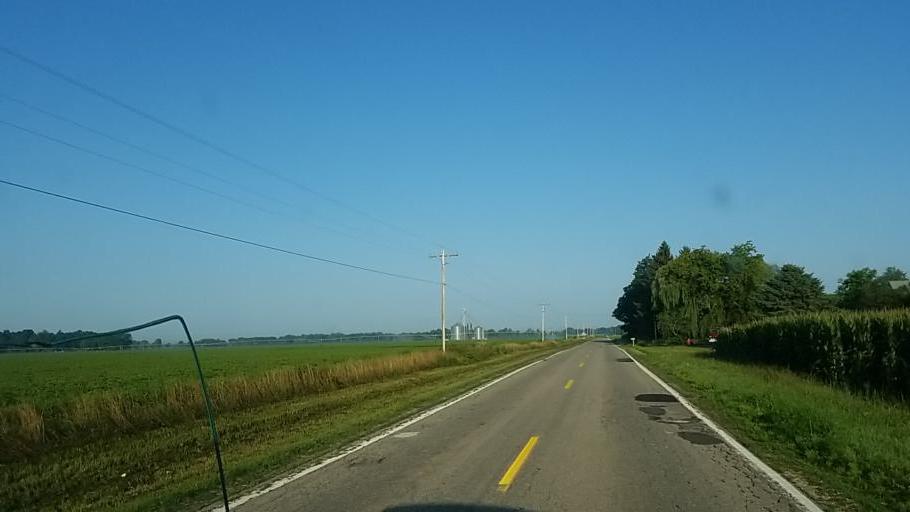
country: US
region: Michigan
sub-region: Montcalm County
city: Howard City
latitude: 43.3592
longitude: -85.3741
